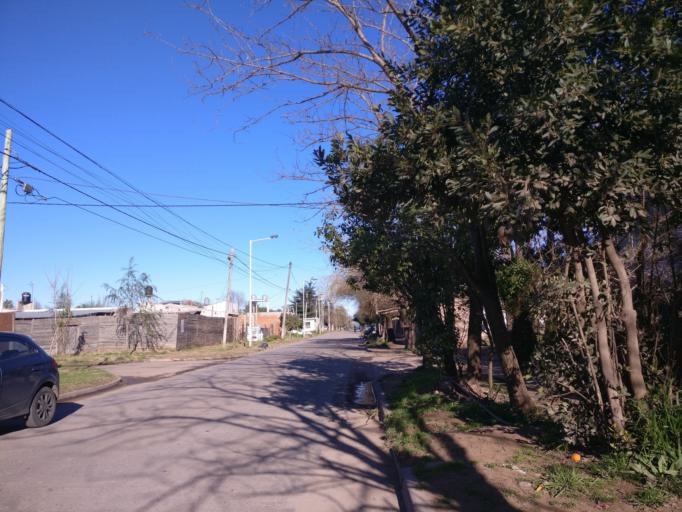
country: AR
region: Buenos Aires
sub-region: Partido de Ezeiza
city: Ezeiza
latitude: -34.9396
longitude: -58.6102
